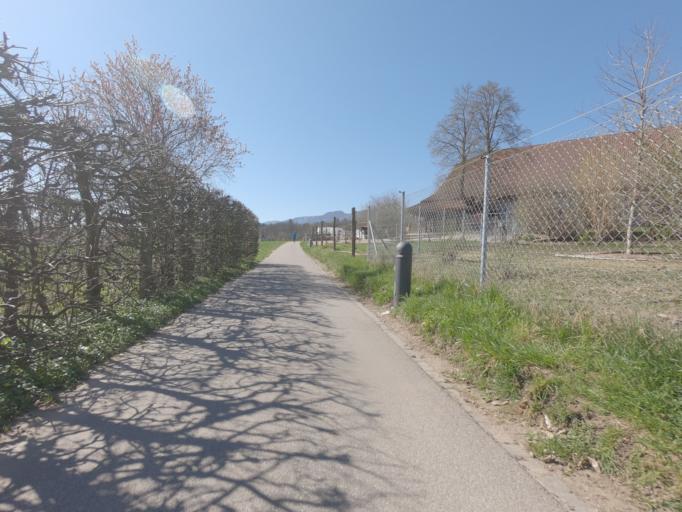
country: CH
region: Solothurn
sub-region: Bezirk Solothurn
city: Solothurn
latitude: 47.2200
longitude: 7.5506
